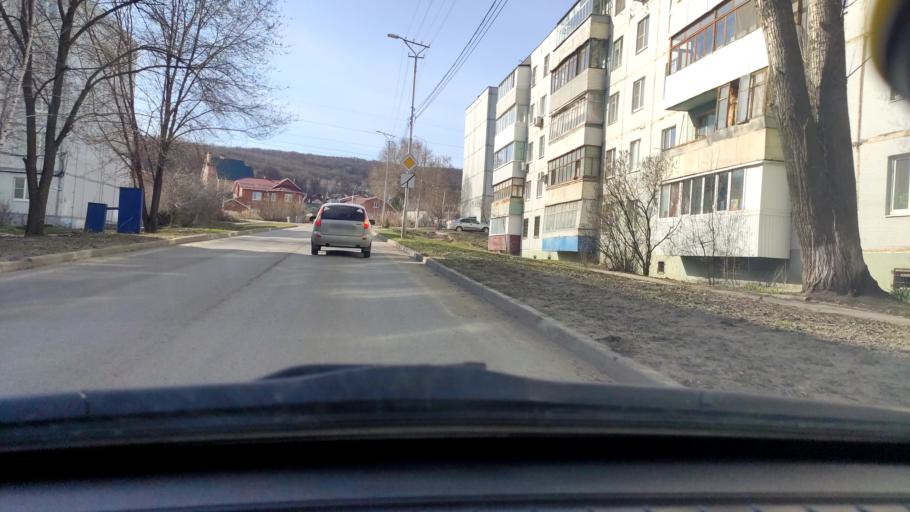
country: RU
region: Samara
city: Zhigulevsk
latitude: 53.3956
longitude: 49.4974
